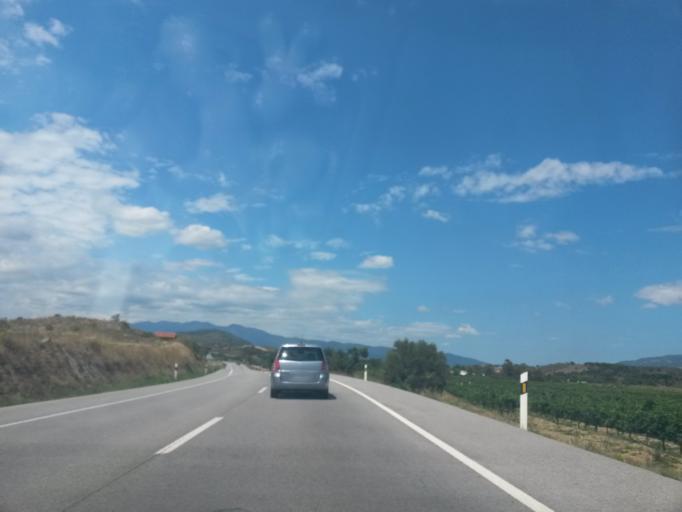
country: ES
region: Catalonia
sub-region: Provincia de Girona
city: Pont de Molins
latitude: 42.3295
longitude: 2.9299
